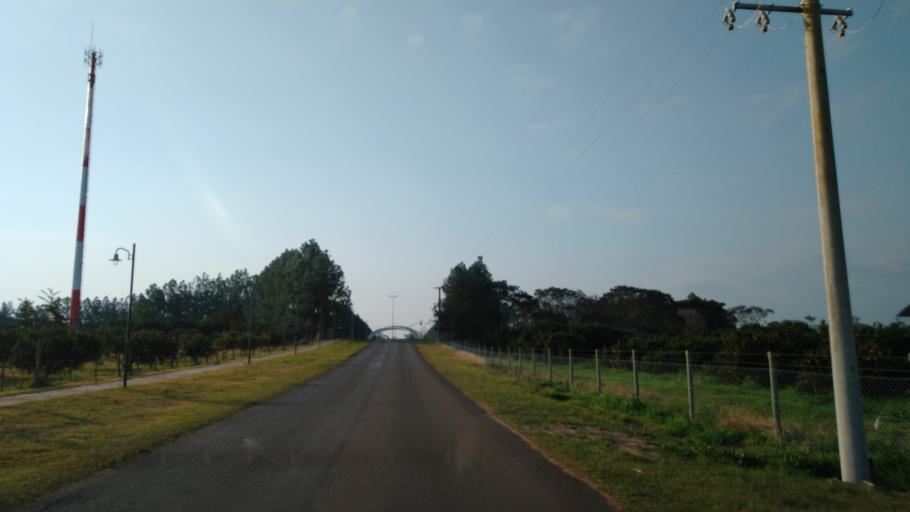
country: AR
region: Entre Rios
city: Santa Ana
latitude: -30.9019
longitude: -57.9246
